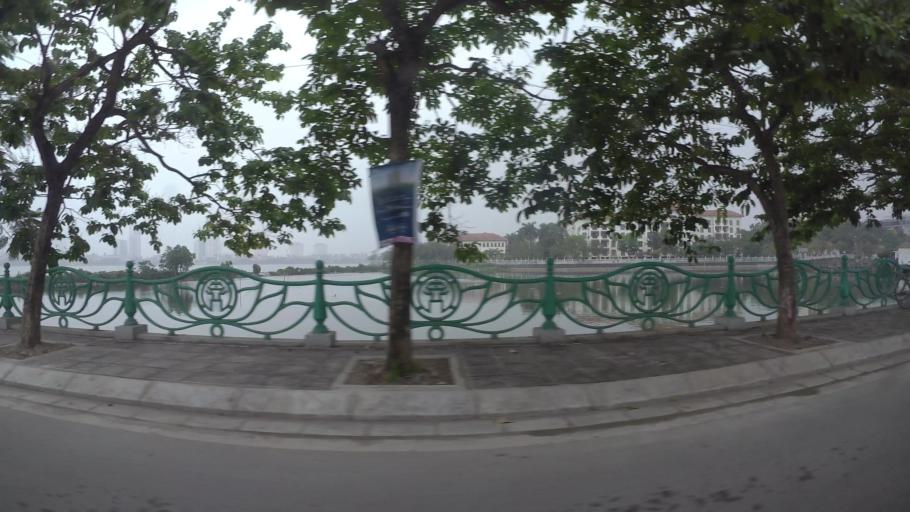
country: VN
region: Ha Noi
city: Tay Ho
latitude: 21.0648
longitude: 105.8205
